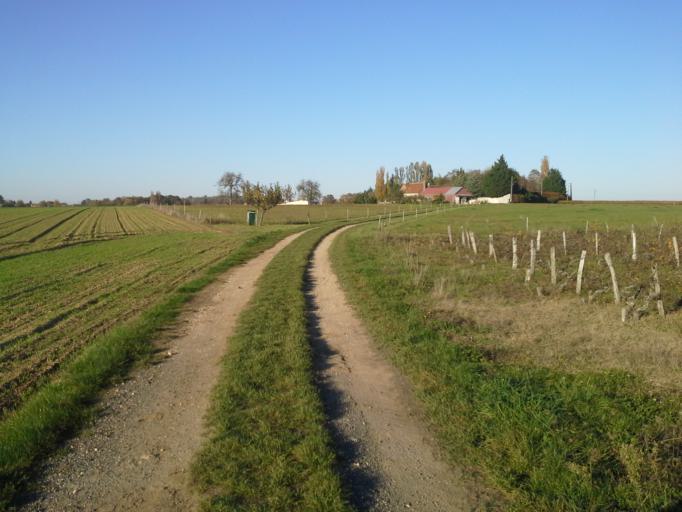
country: FR
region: Centre
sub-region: Departement du Loir-et-Cher
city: Saint-Romain-sur-Cher
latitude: 47.3696
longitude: 1.3966
